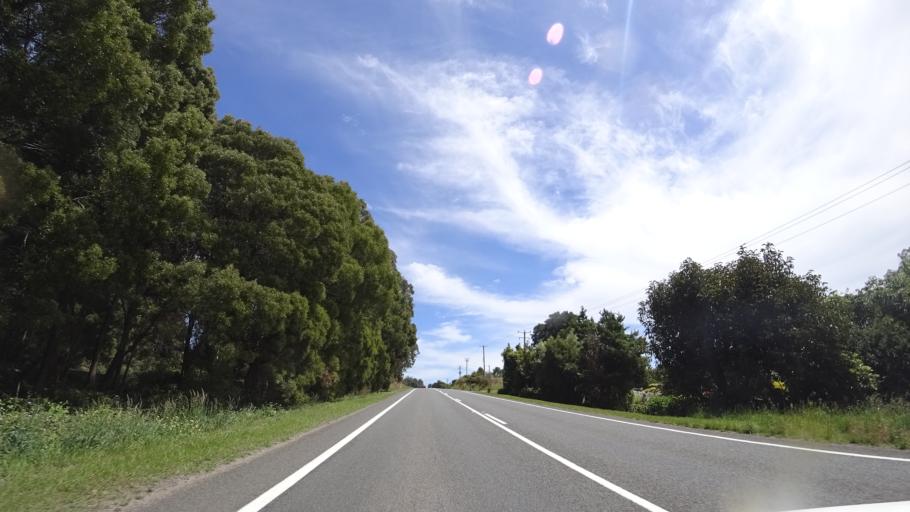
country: AU
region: Tasmania
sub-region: Dorset
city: Scottsdale
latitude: -41.1762
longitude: 147.5400
